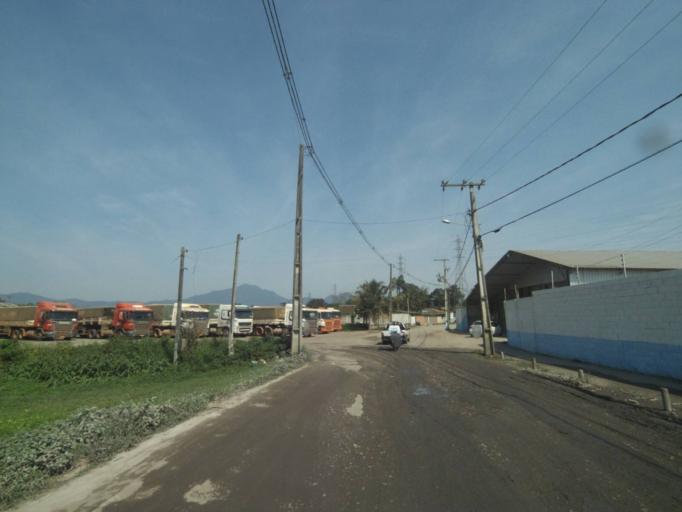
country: BR
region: Parana
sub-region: Paranagua
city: Paranagua
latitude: -25.5511
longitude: -48.5576
